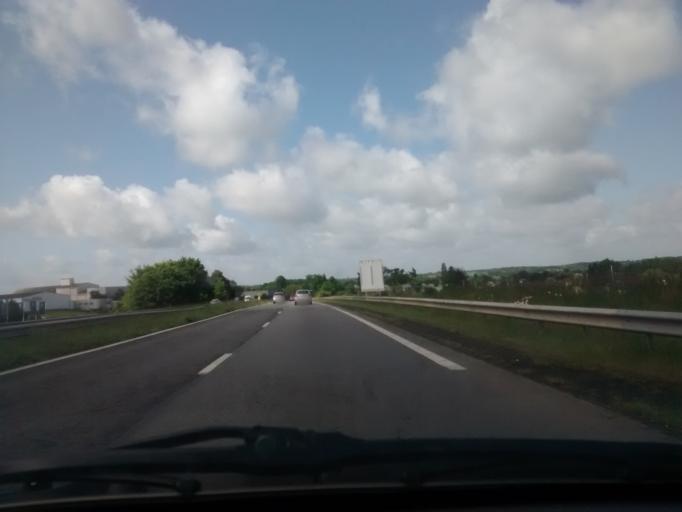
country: FR
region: Brittany
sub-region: Departement d'Ille-et-Vilaine
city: Breal-sous-Montfort
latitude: 48.0619
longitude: -1.8738
